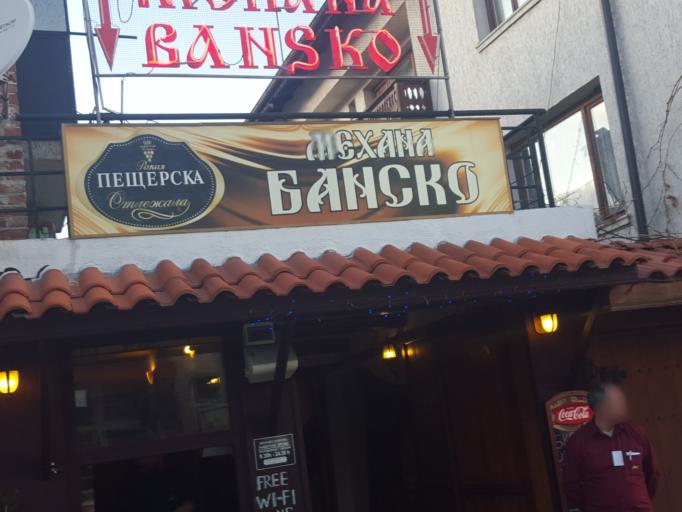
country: BG
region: Blagoevgrad
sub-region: Obshtina Bansko
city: Bansko
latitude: 41.8329
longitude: 23.4842
